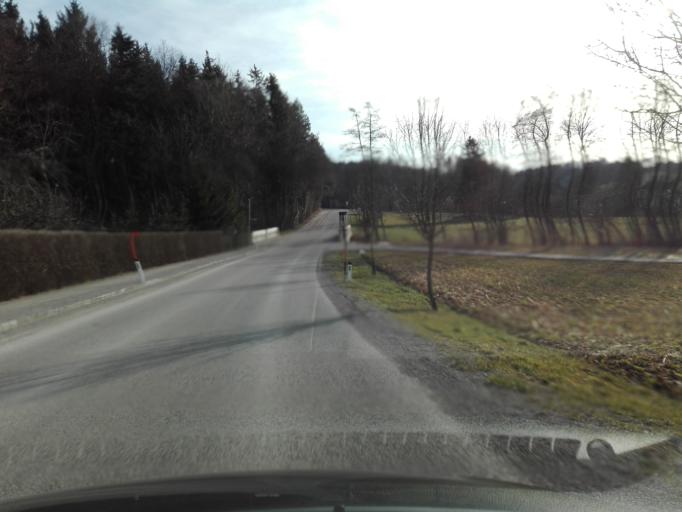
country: AT
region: Lower Austria
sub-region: Politischer Bezirk Amstetten
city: Amstetten
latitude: 48.1638
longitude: 14.8433
